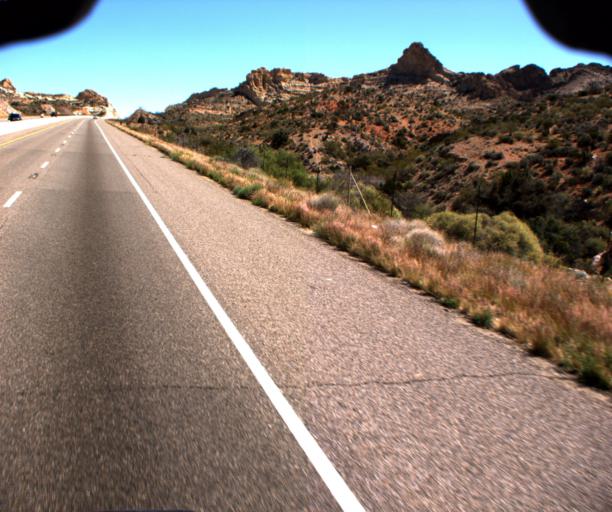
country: US
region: Arizona
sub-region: Mohave County
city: Golden Valley
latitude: 35.2142
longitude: -114.3972
